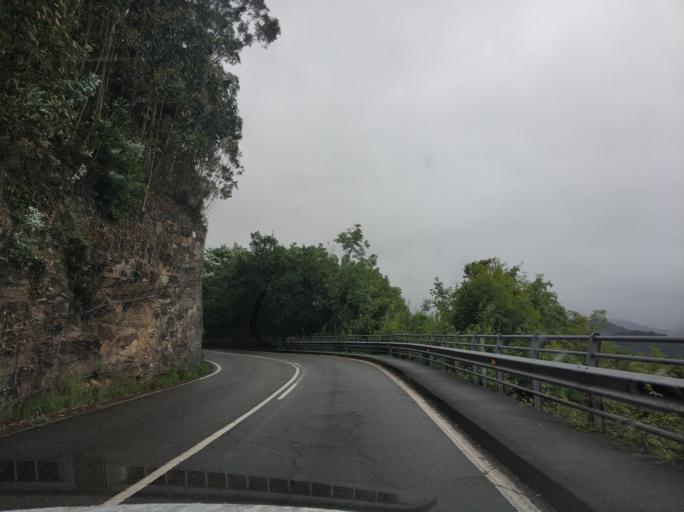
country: ES
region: Asturias
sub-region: Province of Asturias
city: Navia
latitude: 43.5392
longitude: -6.5339
